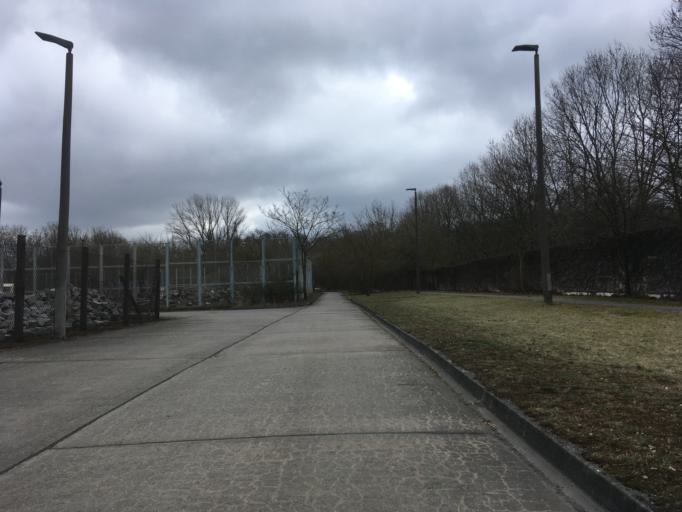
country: DE
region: Berlin
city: Friedrichsfelde
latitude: 52.5083
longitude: 13.5303
